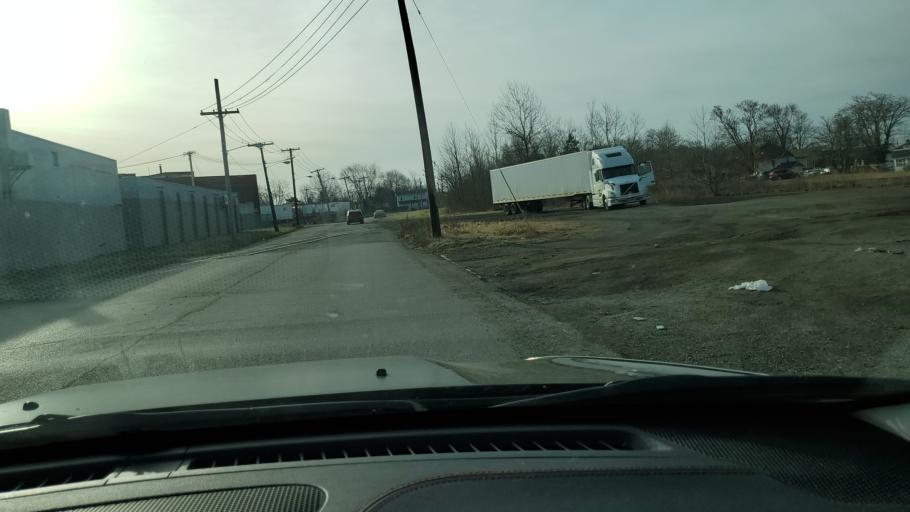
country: US
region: Ohio
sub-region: Trumbull County
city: Niles
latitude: 41.1810
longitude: -80.7572
